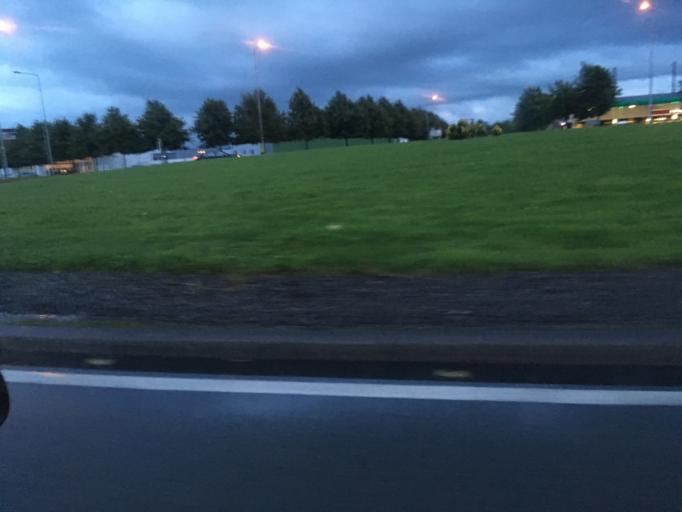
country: IE
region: Leinster
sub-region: Kildare
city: Droichead Nua
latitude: 53.2082
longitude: -6.7431
